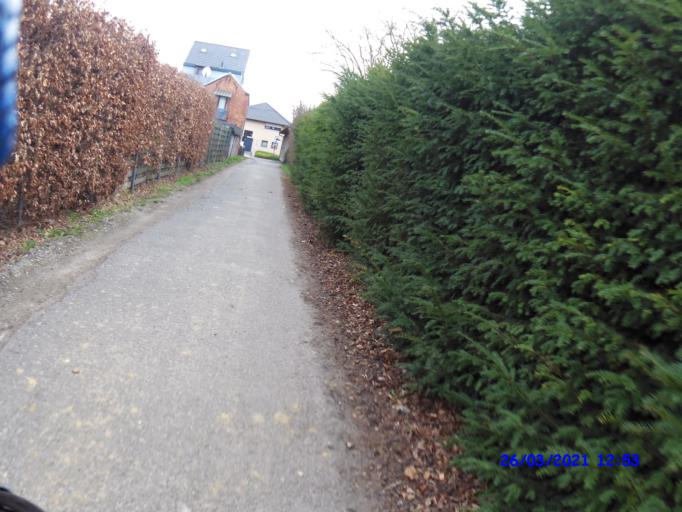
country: BE
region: Flanders
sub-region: Provincie Oost-Vlaanderen
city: Buggenhout
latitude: 51.0112
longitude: 4.1888
